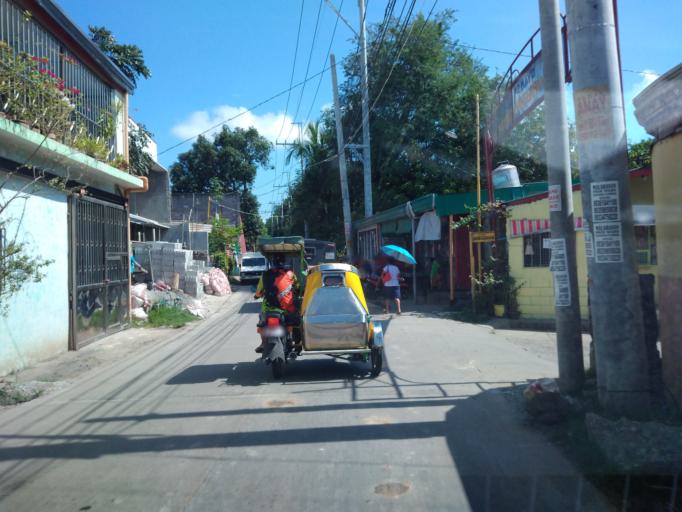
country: PH
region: Central Luzon
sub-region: Province of Bulacan
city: Balasing
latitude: 14.8532
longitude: 121.0110
